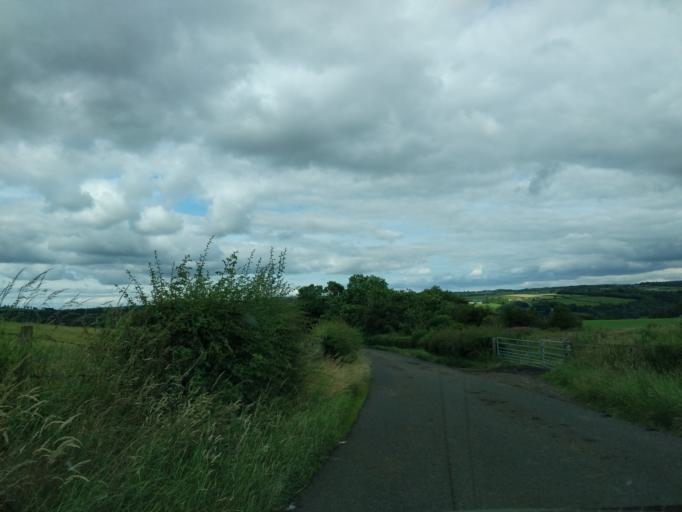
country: GB
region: Scotland
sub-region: South Lanarkshire
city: Dalserf
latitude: 55.7117
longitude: -3.8987
